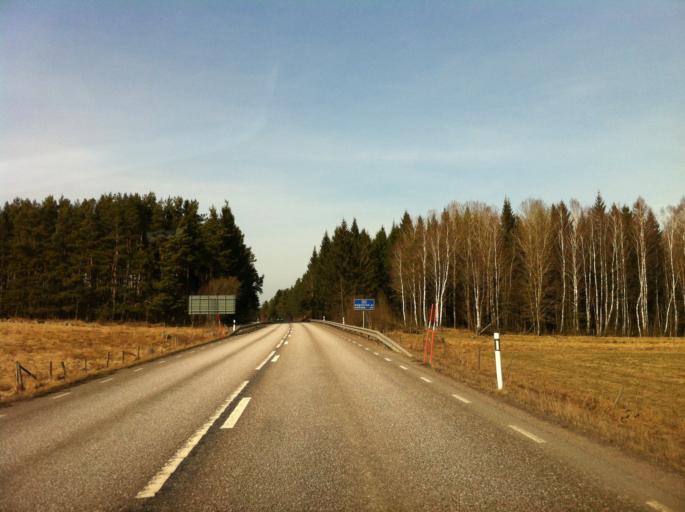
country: SE
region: Vaestra Goetaland
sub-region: Tidaholms Kommun
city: Tidaholm
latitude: 58.1964
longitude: 13.8910
